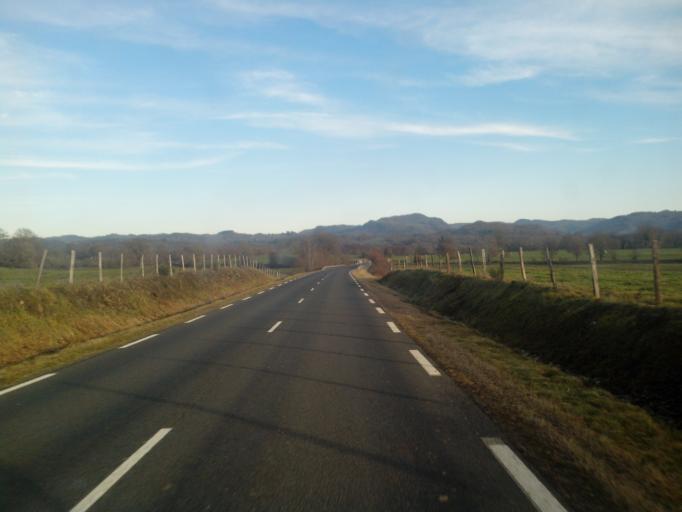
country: FR
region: Auvergne
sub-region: Departement du Cantal
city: Ydes
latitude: 45.3576
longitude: 2.4892
